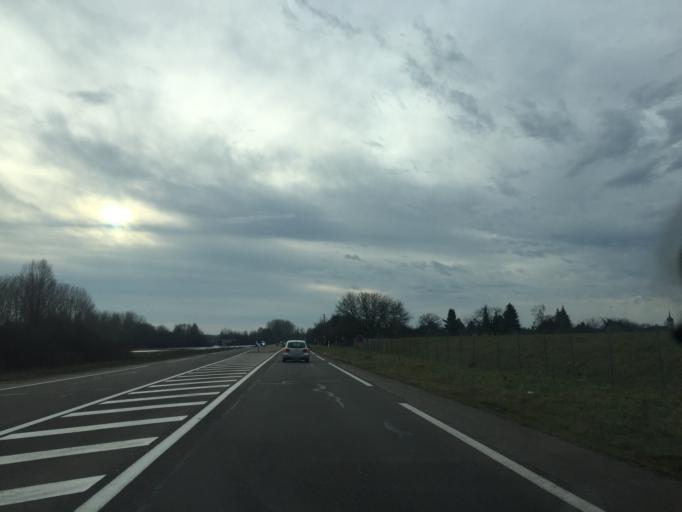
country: FR
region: Franche-Comte
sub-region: Departement du Jura
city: Choisey
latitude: 47.0460
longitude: 5.4451
